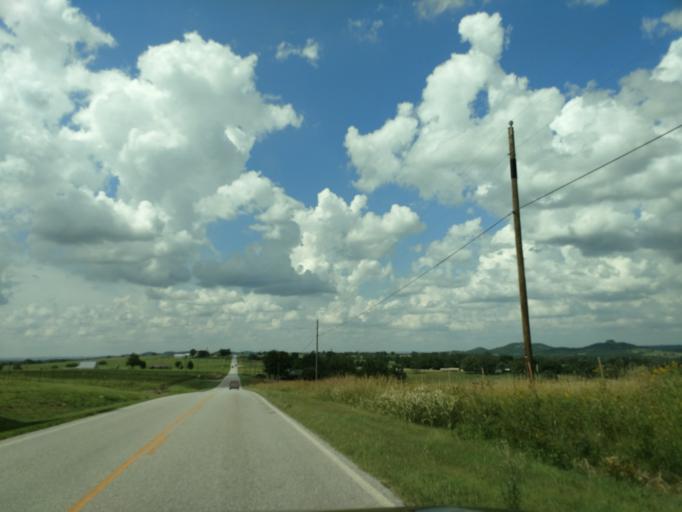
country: US
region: Arkansas
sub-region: Carroll County
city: Berryville
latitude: 36.4489
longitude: -93.5560
